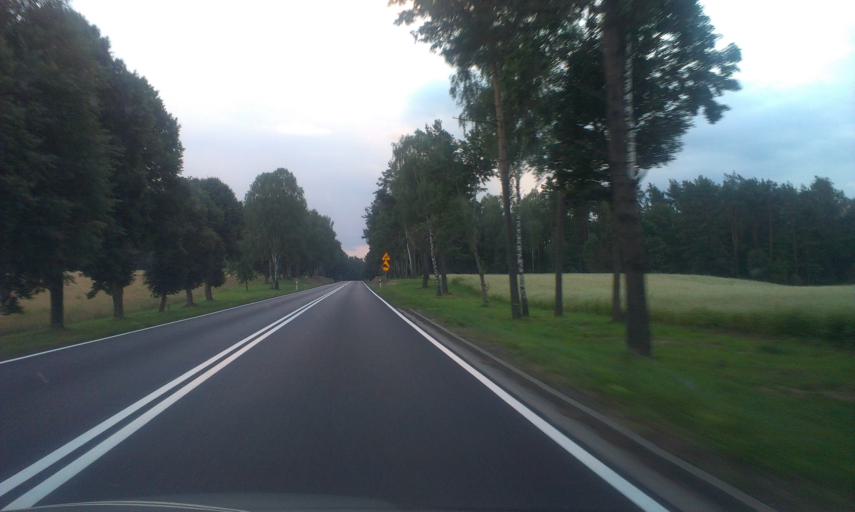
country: PL
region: West Pomeranian Voivodeship
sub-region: Powiat koszalinski
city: Bobolice
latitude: 54.0143
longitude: 16.4981
